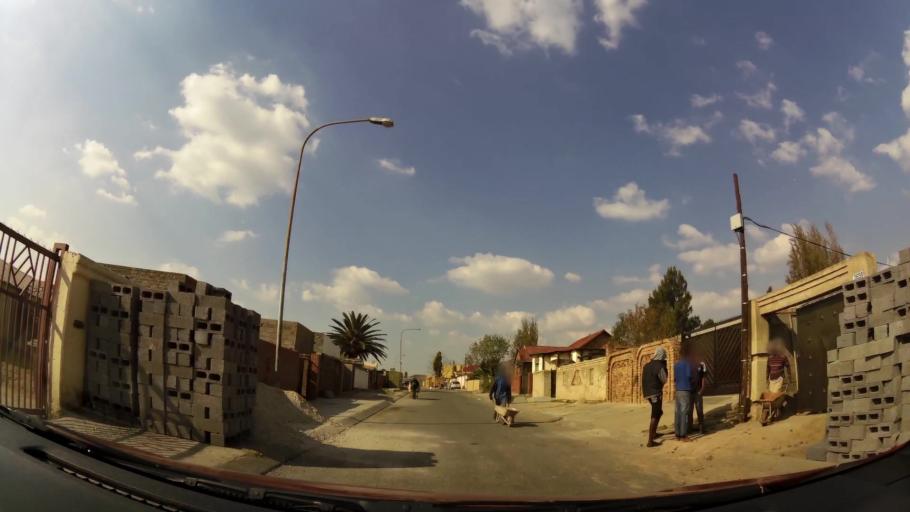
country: ZA
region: Gauteng
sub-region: City of Johannesburg Metropolitan Municipality
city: Soweto
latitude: -26.2354
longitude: 27.9442
